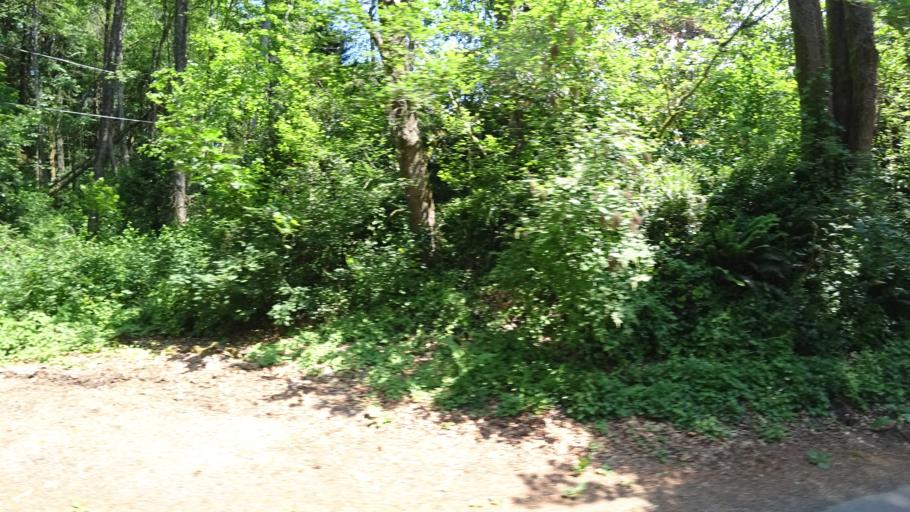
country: US
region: Oregon
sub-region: Washington County
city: West Haven-Sylvan
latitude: 45.5214
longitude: -122.7261
